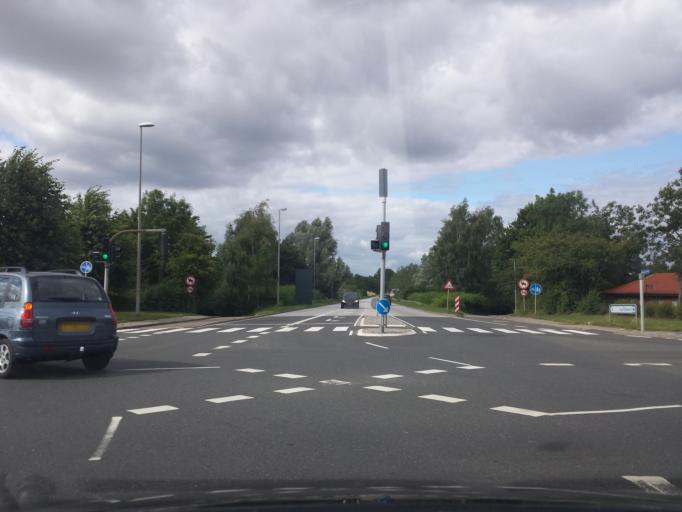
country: DK
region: South Denmark
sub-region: Sonderborg Kommune
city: Sonderborg
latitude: 54.9240
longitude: 9.8082
